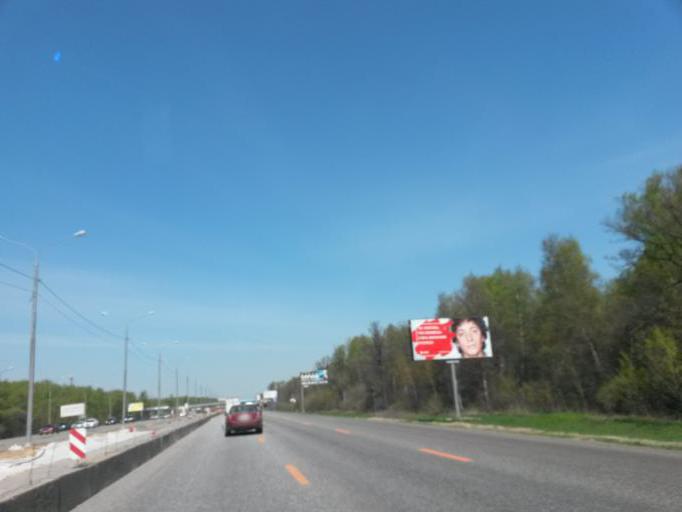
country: RU
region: Moskovskaya
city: Shcherbinka
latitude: 55.4975
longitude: 37.6104
